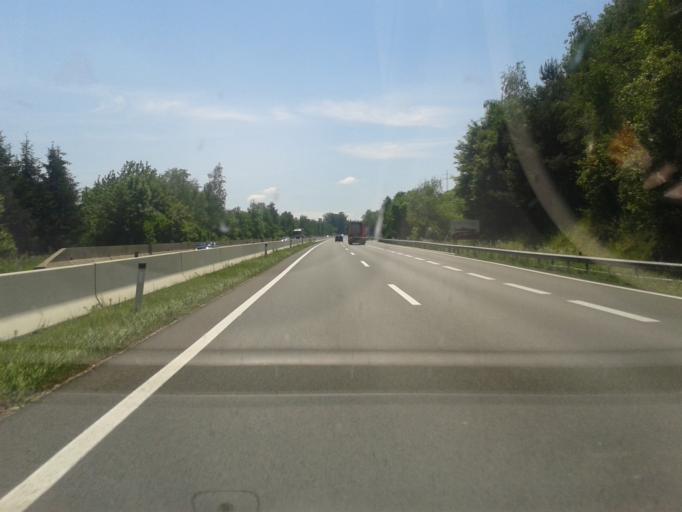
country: AT
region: Carinthia
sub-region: Politischer Bezirk Wolfsberg
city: Sankt Andrae
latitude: 46.7618
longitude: 14.8144
